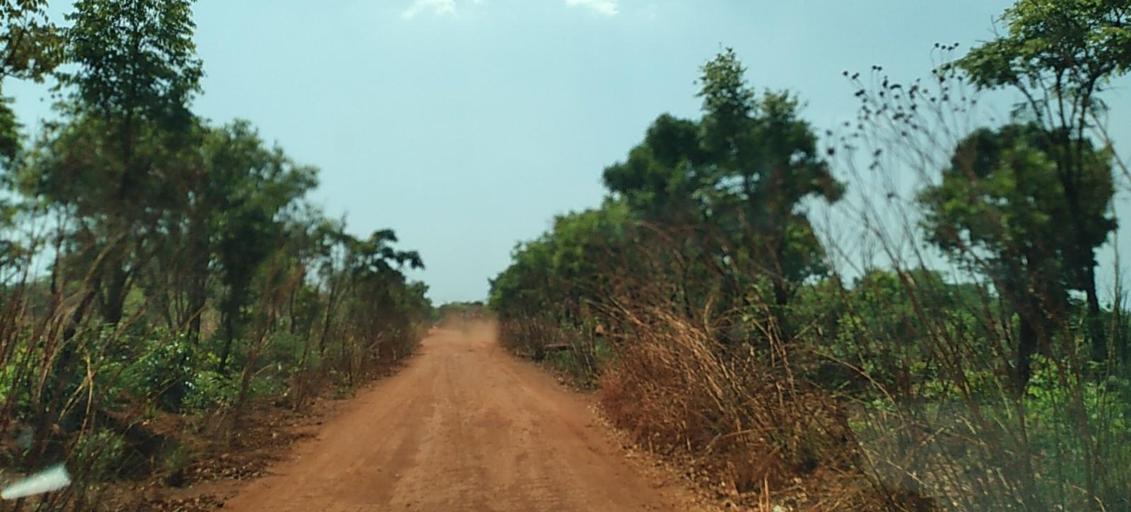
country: ZM
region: North-Western
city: Solwezi
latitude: -12.1269
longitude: 26.3086
